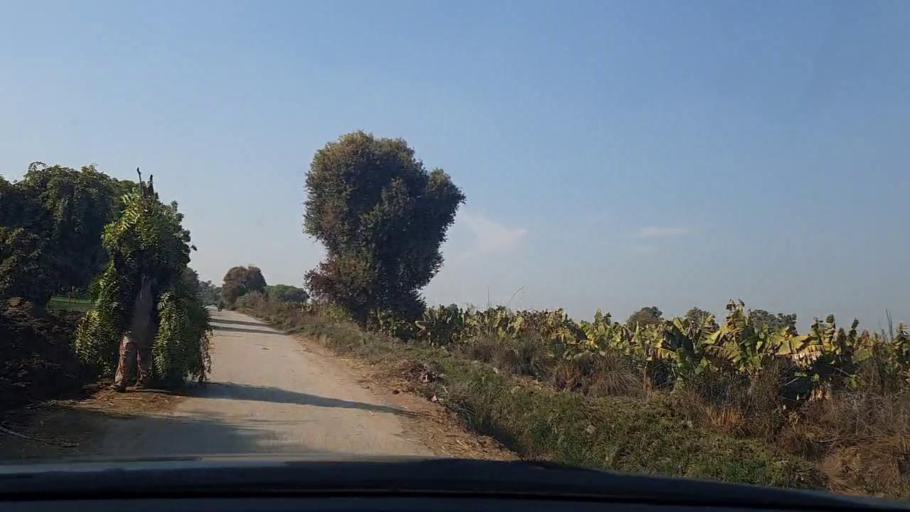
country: PK
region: Sindh
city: Daulatpur
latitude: 26.3060
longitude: 68.0870
